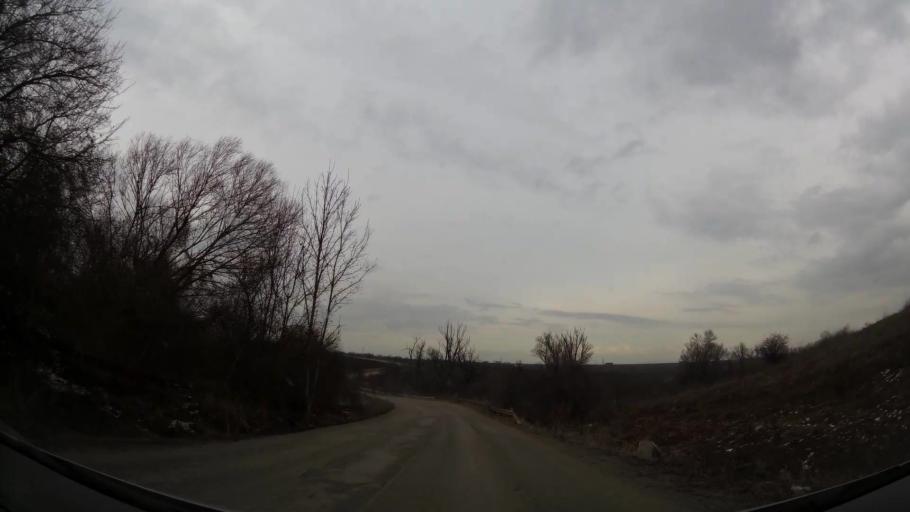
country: BG
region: Sofiya
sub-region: Obshtina Bozhurishte
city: Bozhurishte
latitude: 42.7022
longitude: 23.2204
